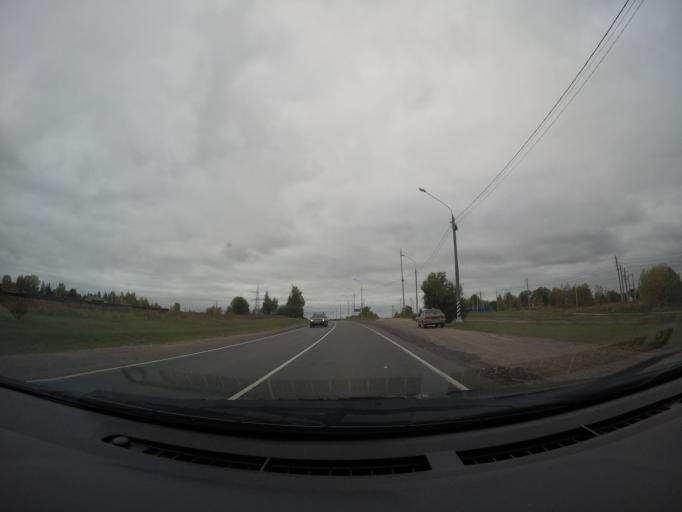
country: RU
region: Moskovskaya
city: Ruza
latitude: 55.7710
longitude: 36.2646
